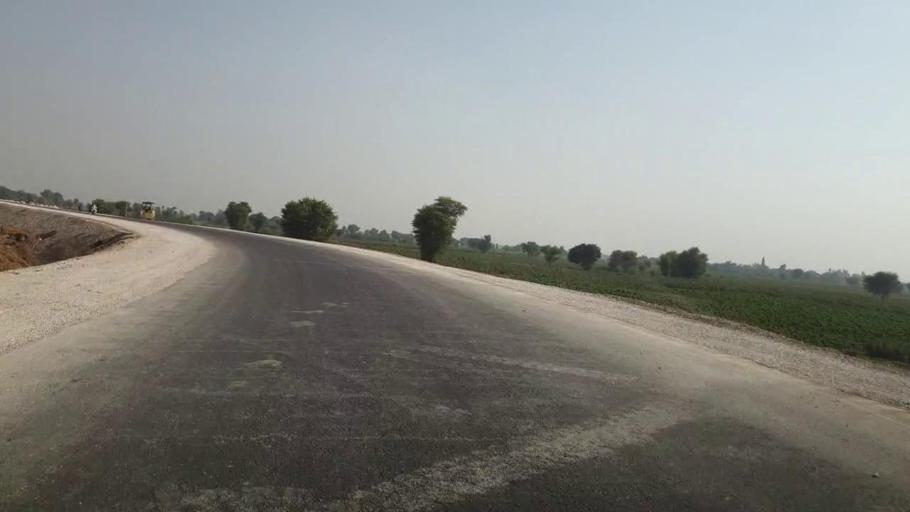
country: PK
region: Sindh
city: Bhan
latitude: 26.5527
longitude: 67.7791
